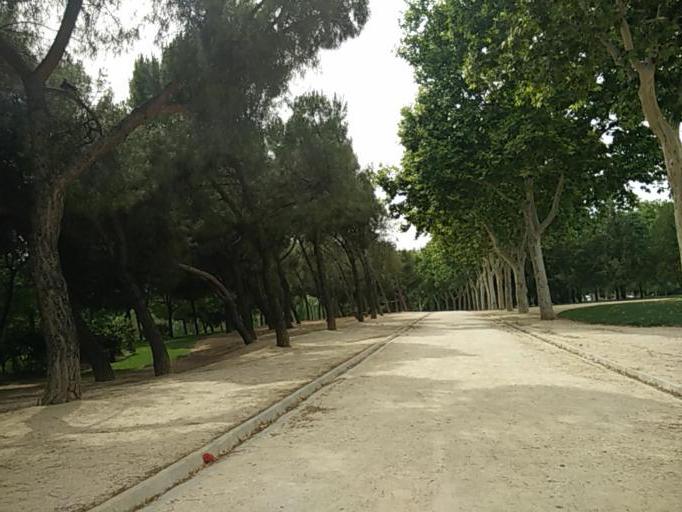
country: ES
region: Madrid
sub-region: Provincia de Madrid
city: Carabanchel
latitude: 40.3976
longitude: -3.7263
